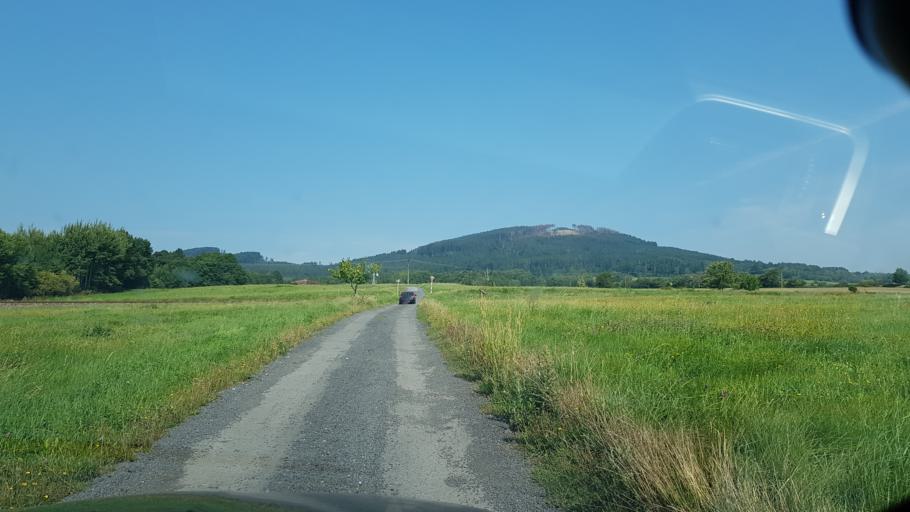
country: CZ
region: Olomoucky
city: Ceska Ves
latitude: 50.2659
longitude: 17.2392
